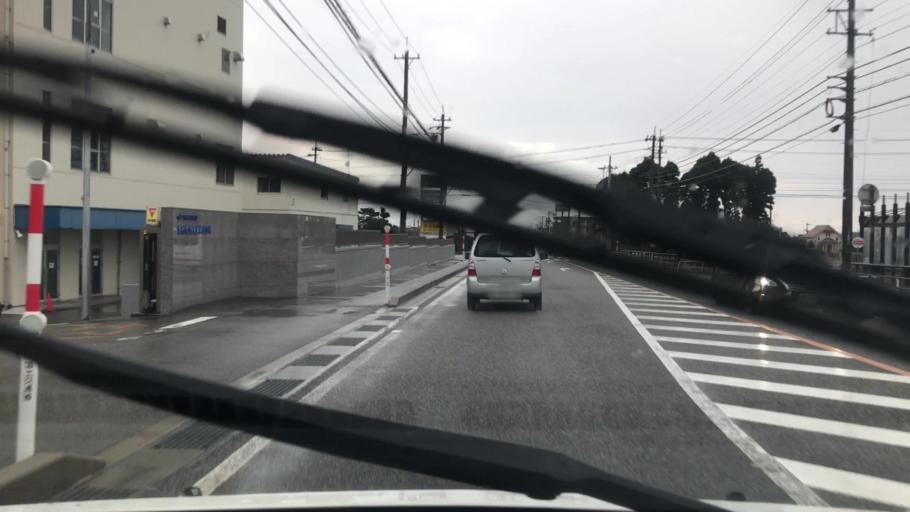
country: JP
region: Toyama
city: Yatsuomachi-higashikumisaka
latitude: 36.6096
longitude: 137.2045
